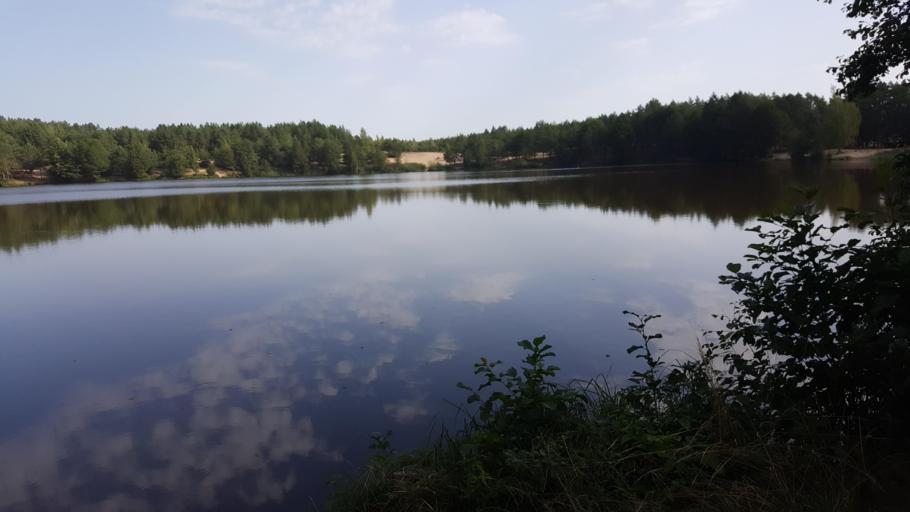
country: BY
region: Brest
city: Ivatsevichy
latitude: 52.7913
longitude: 25.5567
